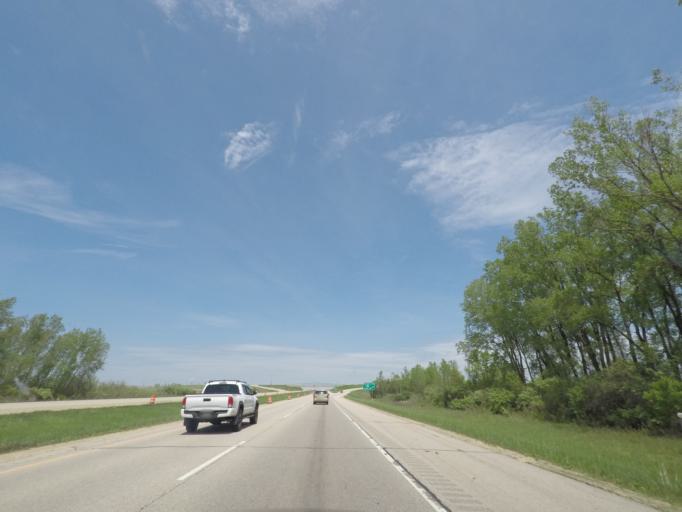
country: US
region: Wisconsin
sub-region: Dane County
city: Madison
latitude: 43.0039
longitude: -89.3840
